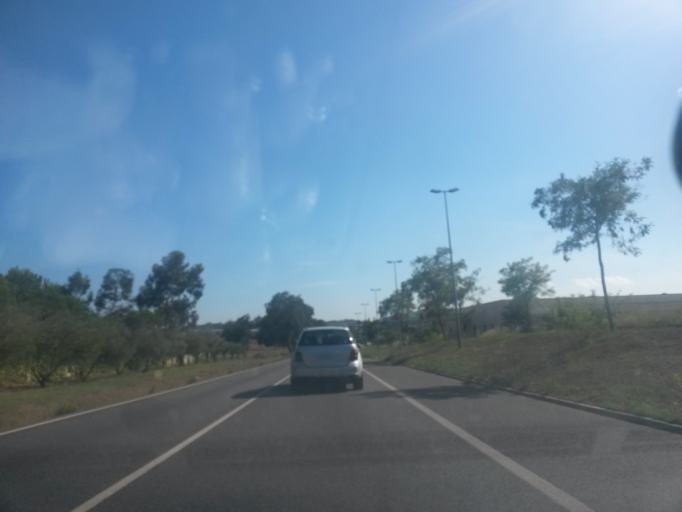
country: ES
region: Catalonia
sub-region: Provincia de Girona
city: Regencos
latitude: 41.9381
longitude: 3.1612
